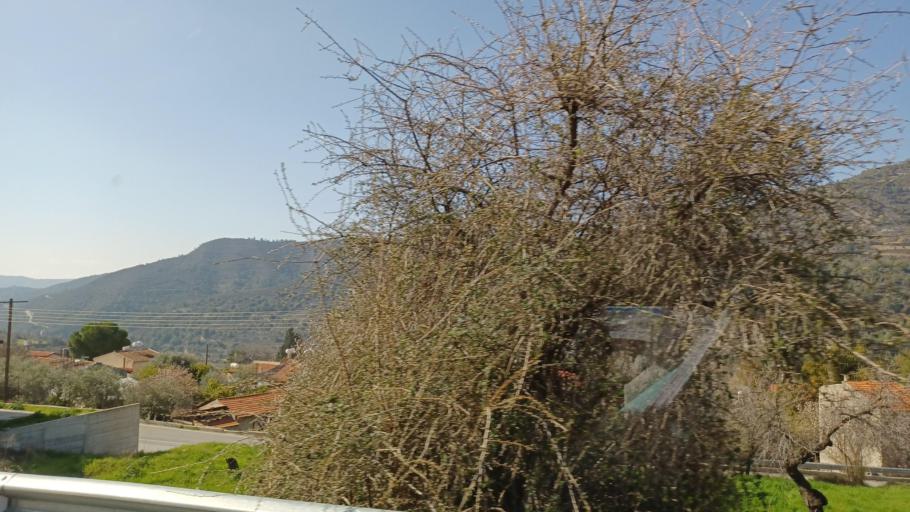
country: CY
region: Limassol
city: Pelendri
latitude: 34.8104
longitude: 32.9115
